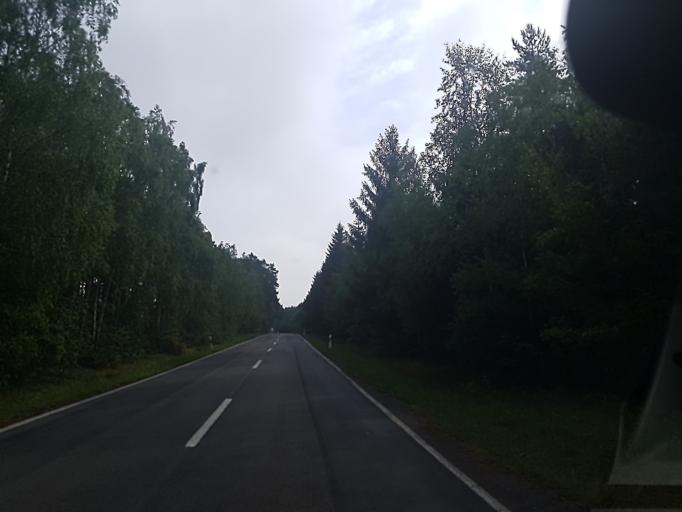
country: DE
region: Brandenburg
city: Gorzke
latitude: 52.0955
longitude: 12.3388
